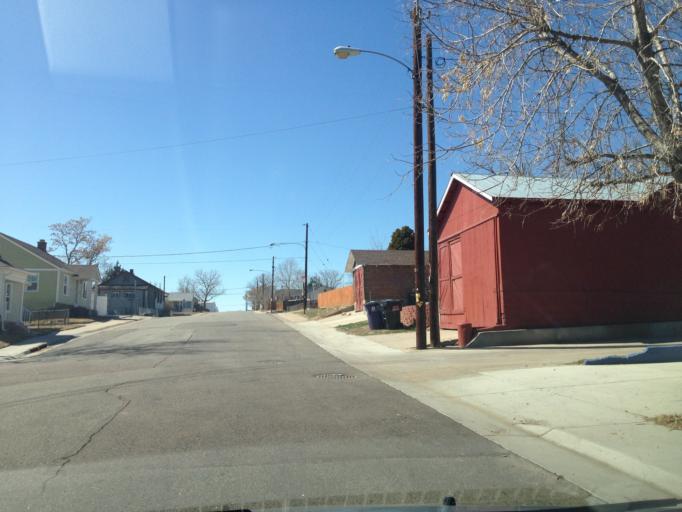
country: US
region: Colorado
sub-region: Adams County
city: Twin Lakes
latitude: 39.7874
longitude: -104.9844
